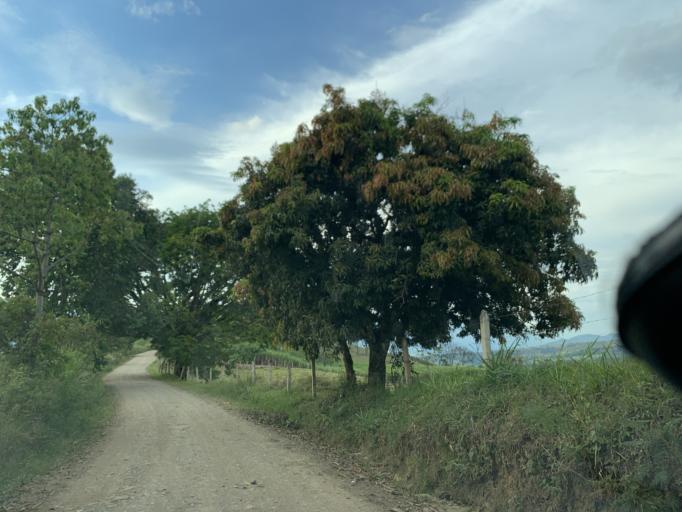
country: CO
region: Boyaca
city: Santana
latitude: 6.0724
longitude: -73.4855
